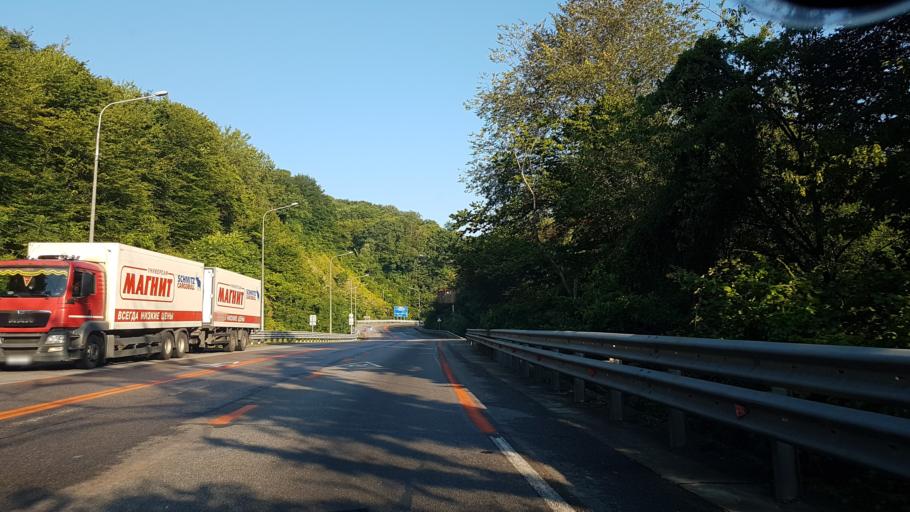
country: RU
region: Krasnodarskiy
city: Dagomys
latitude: 43.6461
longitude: 39.6933
